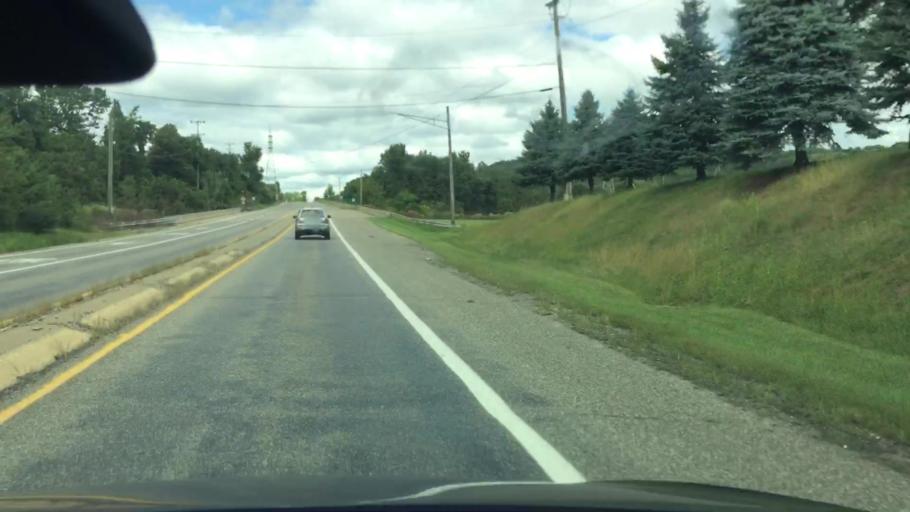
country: US
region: Pennsylvania
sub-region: Allegheny County
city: Cheswick
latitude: 40.5484
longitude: -79.8193
